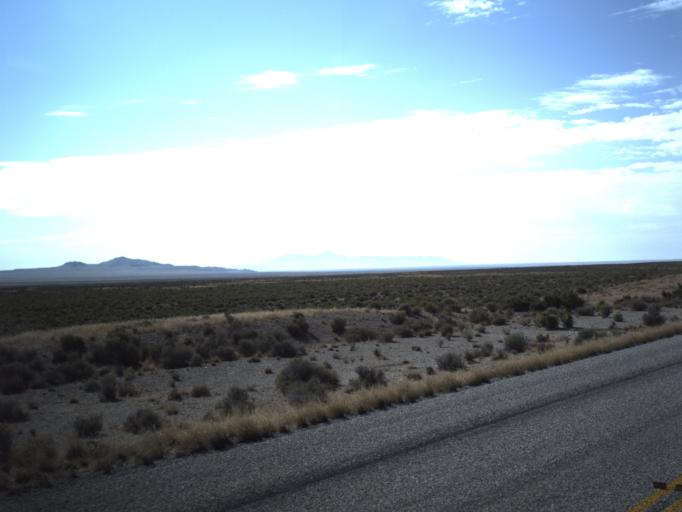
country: US
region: Utah
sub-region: Tooele County
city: Wendover
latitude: 41.5618
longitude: -113.5828
